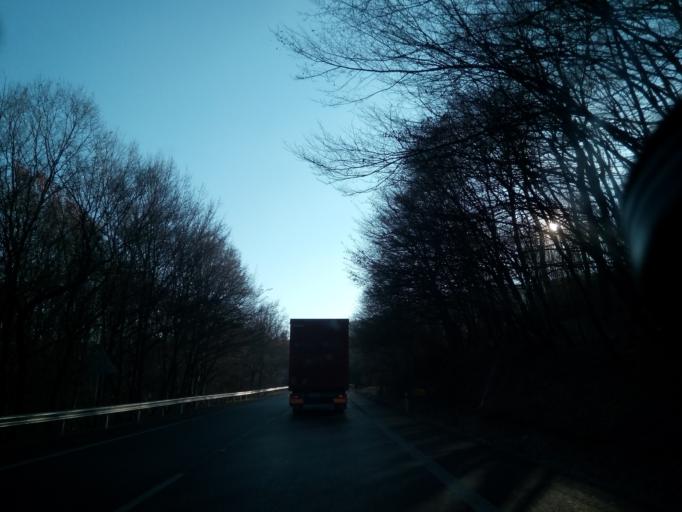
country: SK
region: Kosicky
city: Kosice
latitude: 48.7375
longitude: 21.3684
